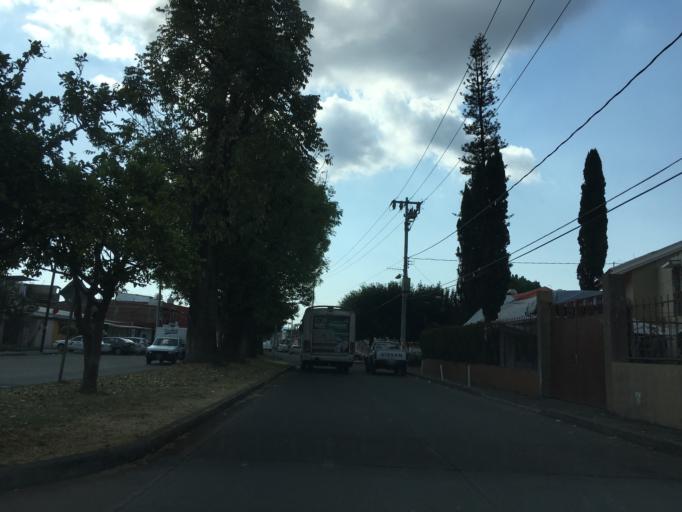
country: MX
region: Michoacan
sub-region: Uruapan
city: Uruapan
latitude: 19.3958
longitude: -102.0517
